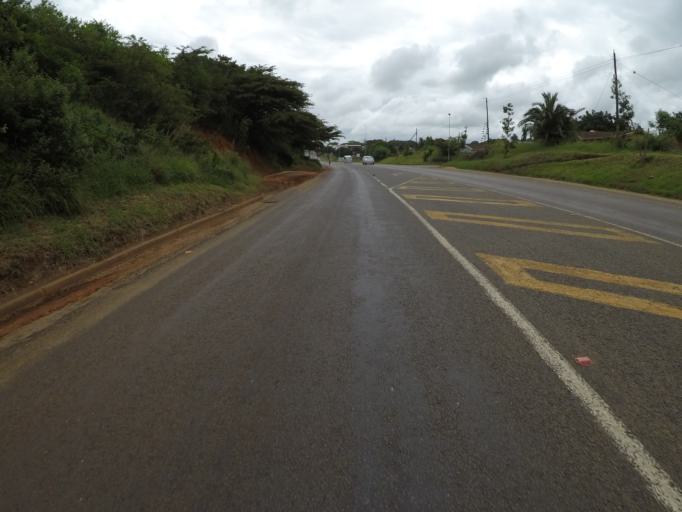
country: ZA
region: KwaZulu-Natal
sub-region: uThungulu District Municipality
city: Empangeni
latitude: -28.7738
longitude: 31.8682
